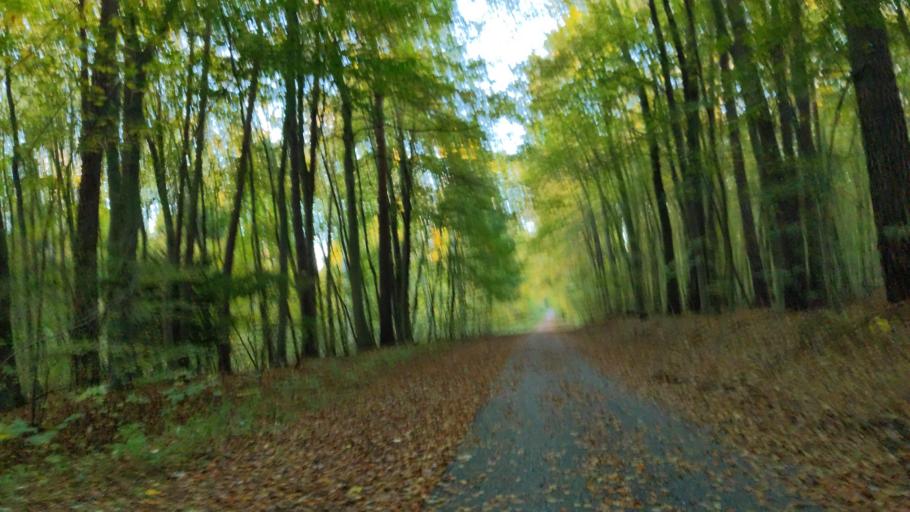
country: DE
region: Schleswig-Holstein
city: Bad Schwartau
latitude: 53.8896
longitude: 10.7515
